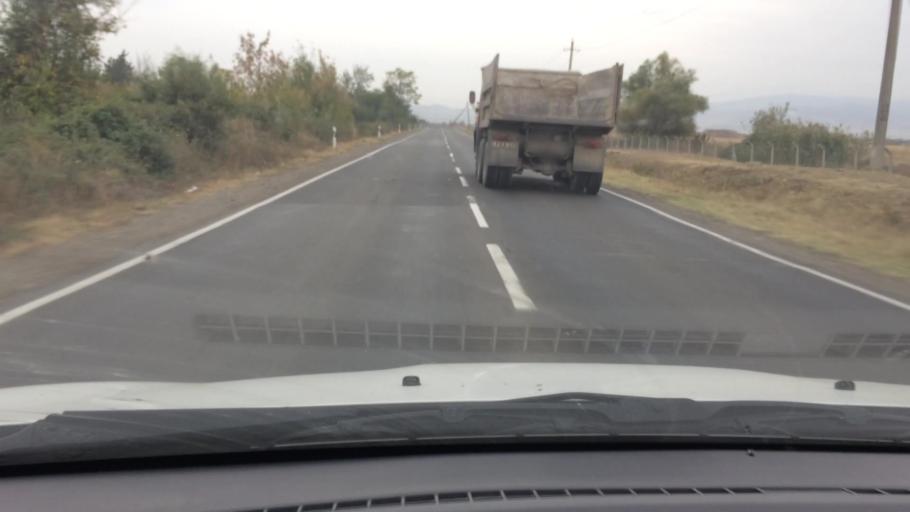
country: GE
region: Kvemo Kartli
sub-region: Marneuli
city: Marneuli
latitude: 41.4681
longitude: 44.8045
